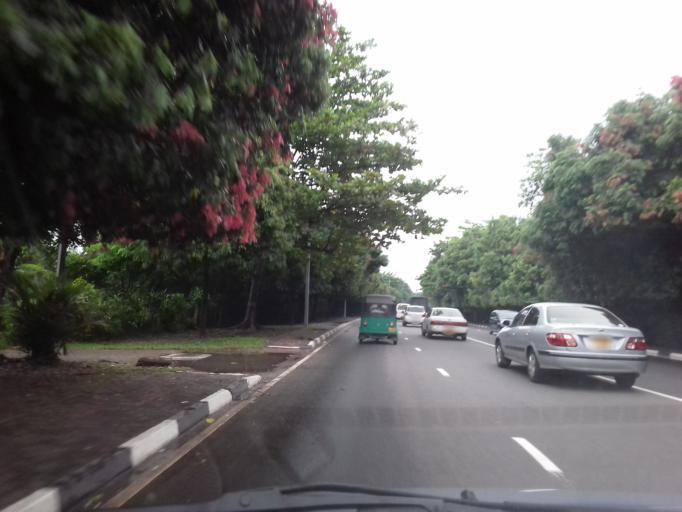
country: LK
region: Western
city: Battaramulla South
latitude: 6.8974
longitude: 79.9142
